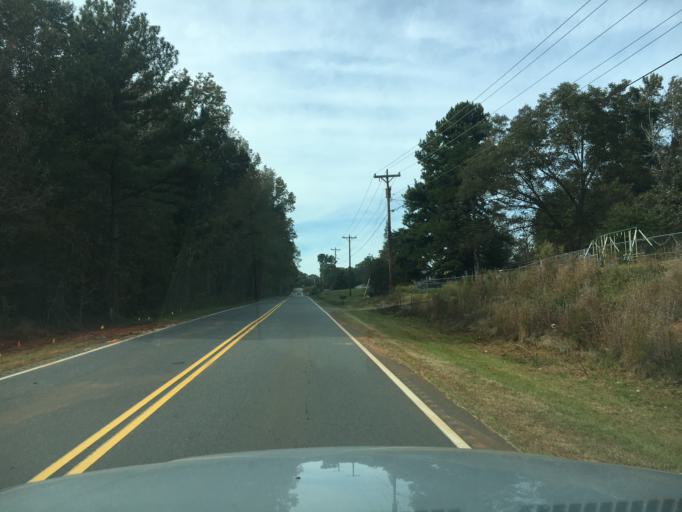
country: US
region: South Carolina
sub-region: Spartanburg County
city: Duncan
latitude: 34.8860
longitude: -82.1293
